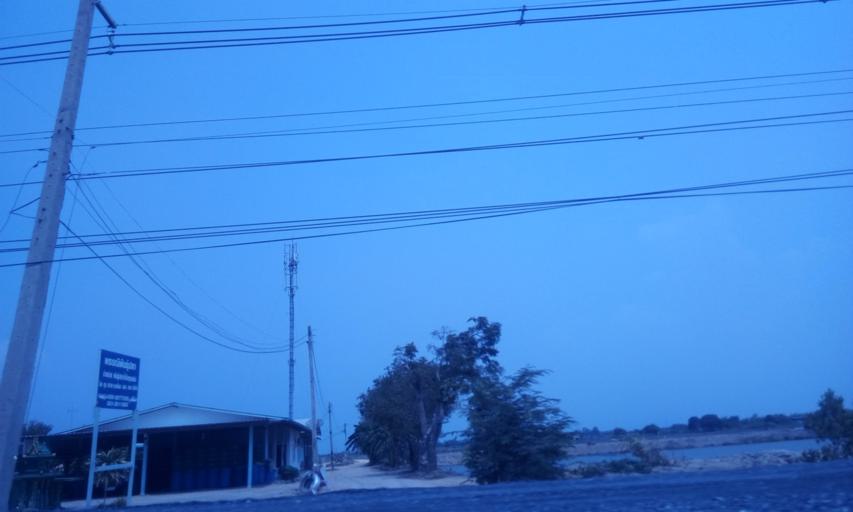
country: TH
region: Chon Buri
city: Phan Thong
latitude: 13.5343
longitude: 101.1493
